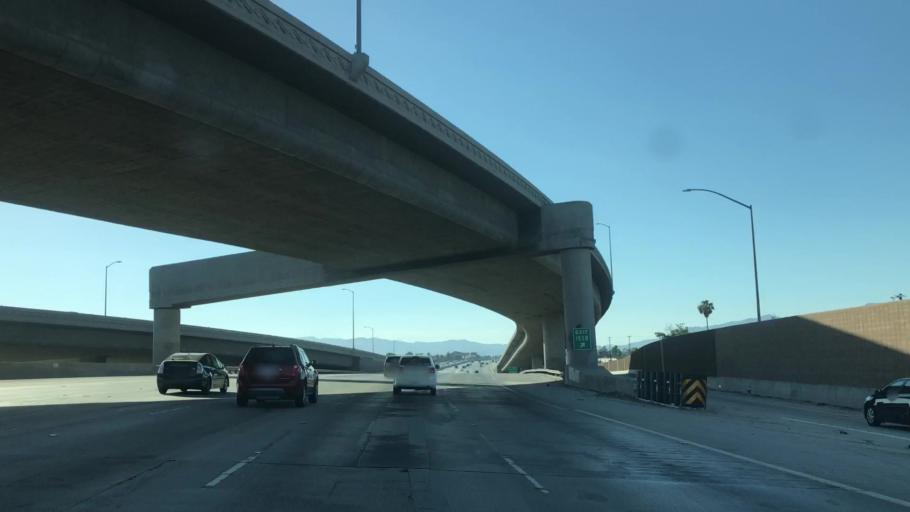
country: US
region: California
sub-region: Los Angeles County
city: San Fernando
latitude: 34.2333
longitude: -118.4093
